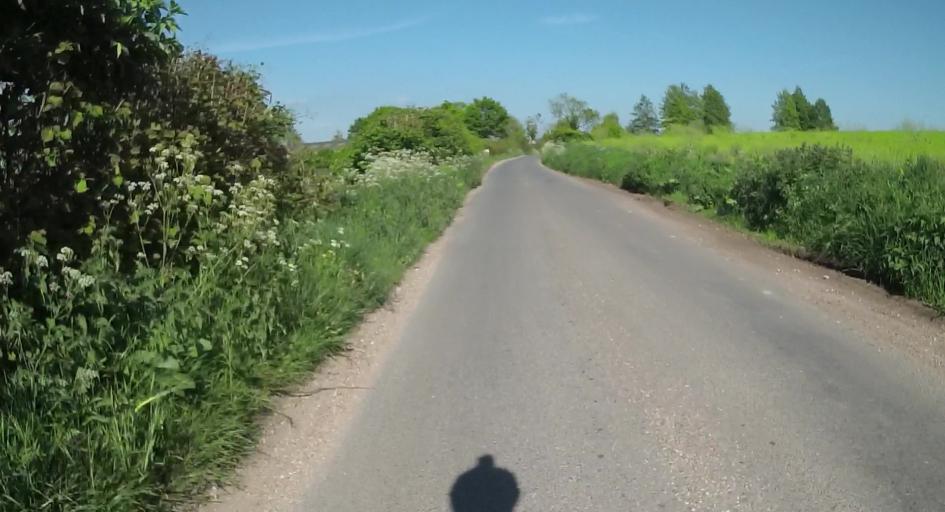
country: GB
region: England
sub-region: Hampshire
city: Kings Worthy
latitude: 51.0834
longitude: -1.2777
